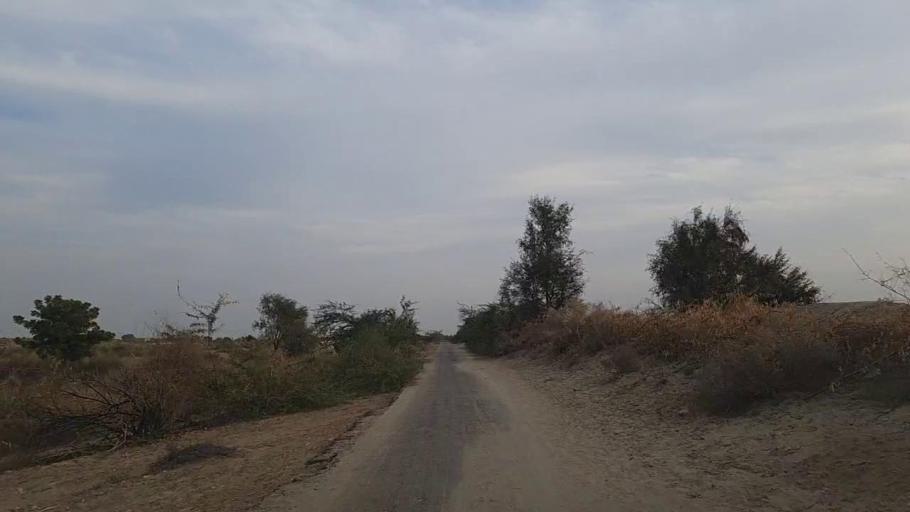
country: PK
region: Sindh
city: Jam Sahib
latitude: 26.4811
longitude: 68.5620
